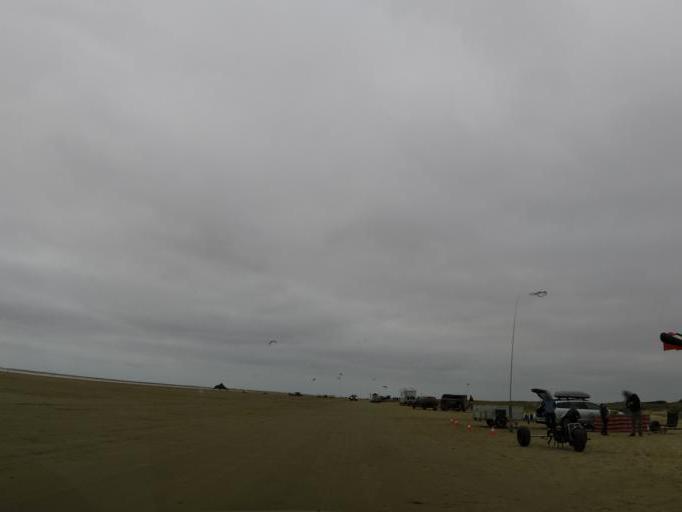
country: DE
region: Schleswig-Holstein
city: List
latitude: 55.0832
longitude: 8.5155
